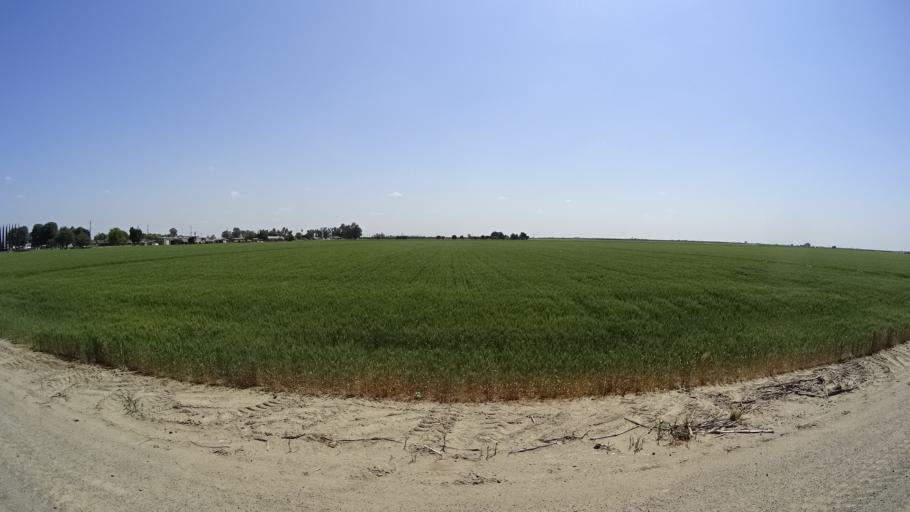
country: US
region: California
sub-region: Kings County
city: Home Garden
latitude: 36.2960
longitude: -119.6190
